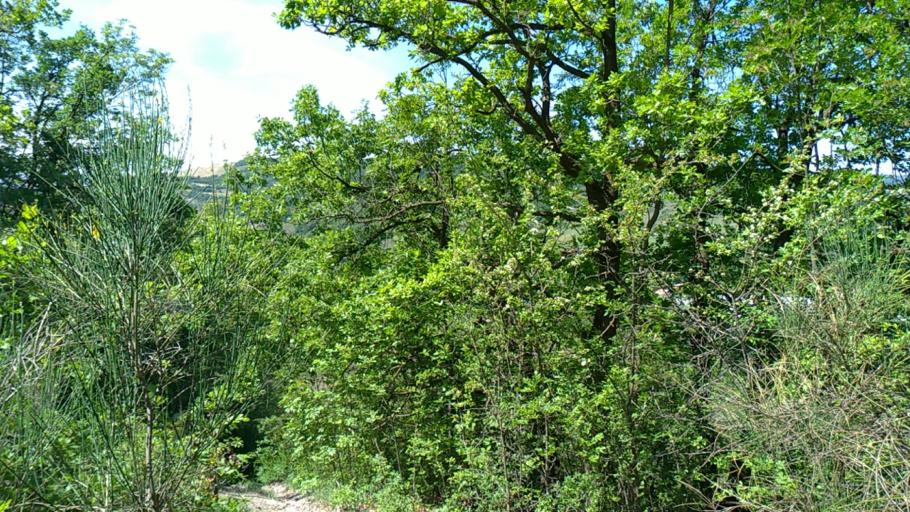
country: IT
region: Emilia-Romagna
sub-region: Provincia di Modena
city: Guiglia
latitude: 44.4122
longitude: 10.9278
